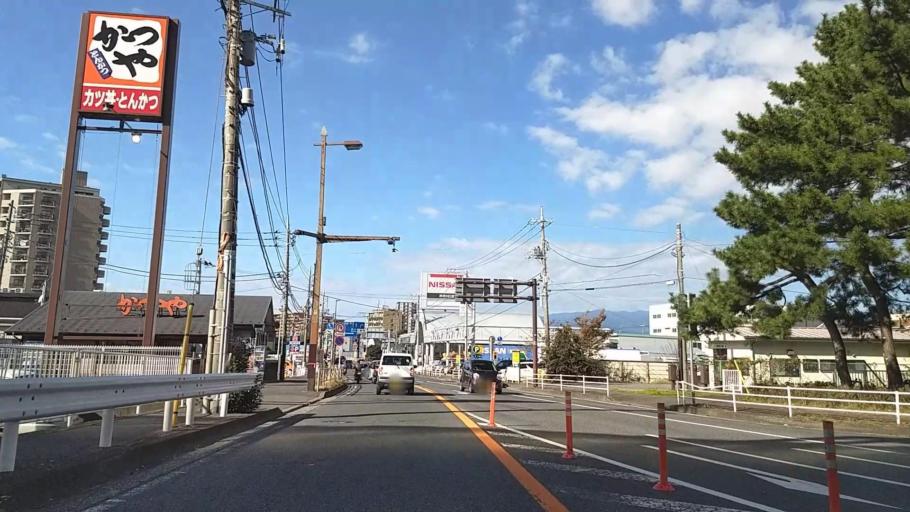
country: JP
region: Kanagawa
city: Chigasaki
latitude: 35.3328
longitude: 139.3836
